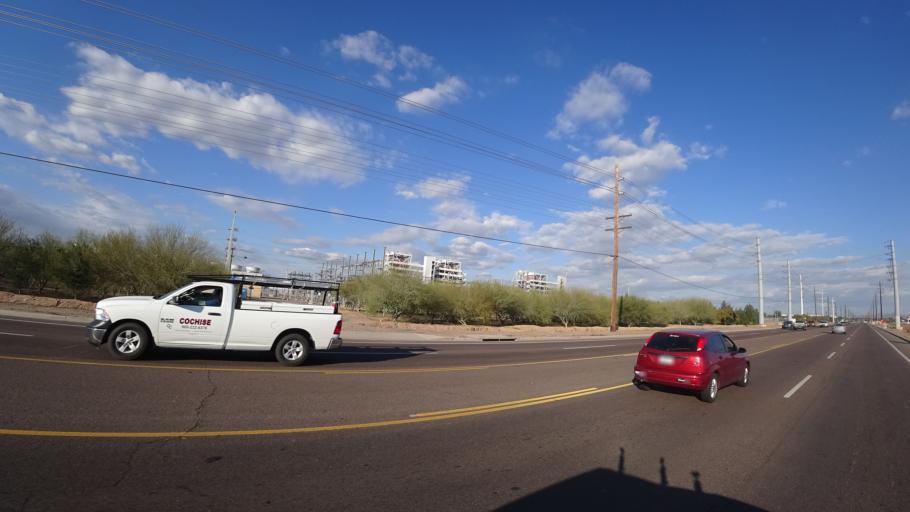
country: US
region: Arizona
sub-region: Maricopa County
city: Peoria
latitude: 33.5524
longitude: -112.2183
